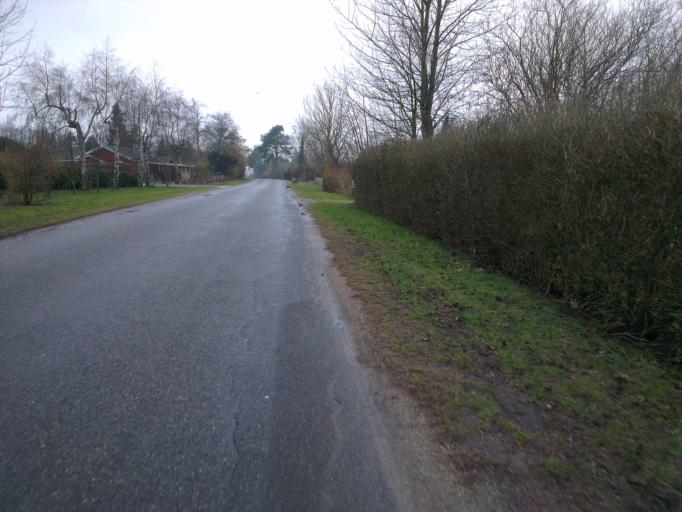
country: DK
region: Capital Region
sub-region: Frederikssund Kommune
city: Jaegerspris
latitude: 55.8332
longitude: 11.9670
